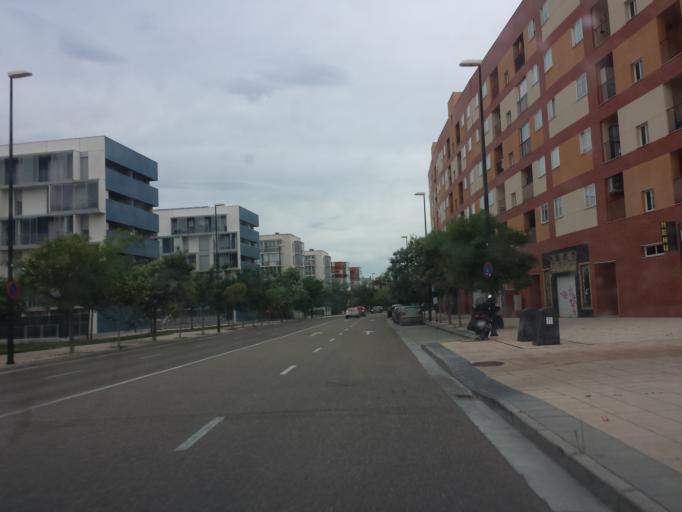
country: ES
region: Aragon
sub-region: Provincia de Zaragoza
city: Montecanal
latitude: 41.6204
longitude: -0.9311
